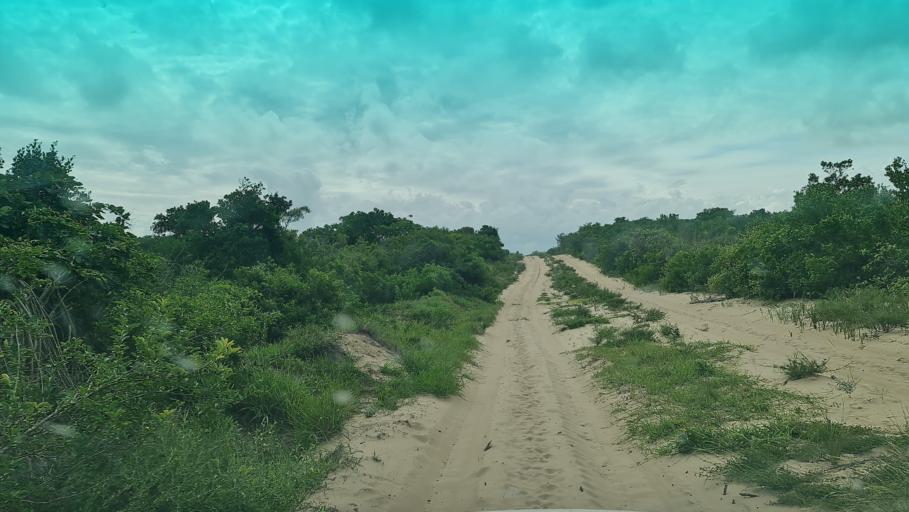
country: MZ
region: Maputo
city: Manhica
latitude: -25.4397
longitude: 32.9267
